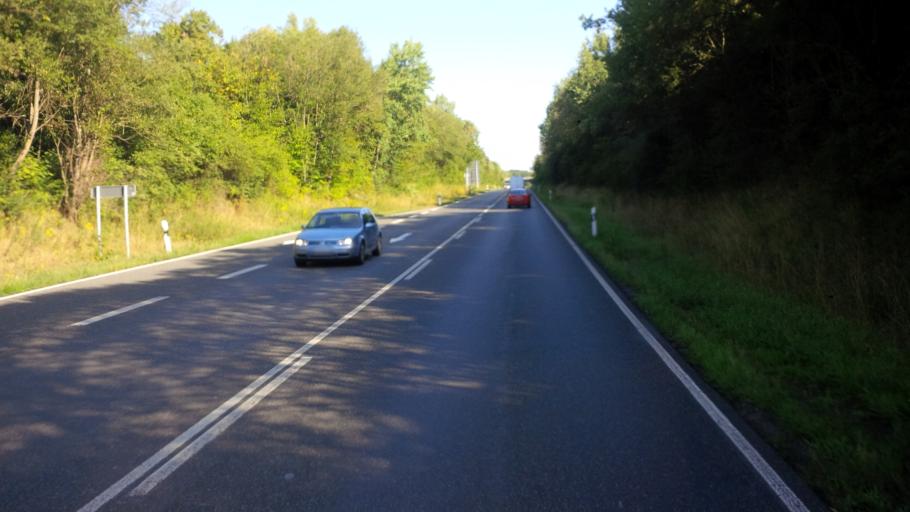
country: DE
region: Hesse
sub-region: Regierungsbezirk Darmstadt
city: Wehrheim
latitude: 50.2998
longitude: 8.5484
